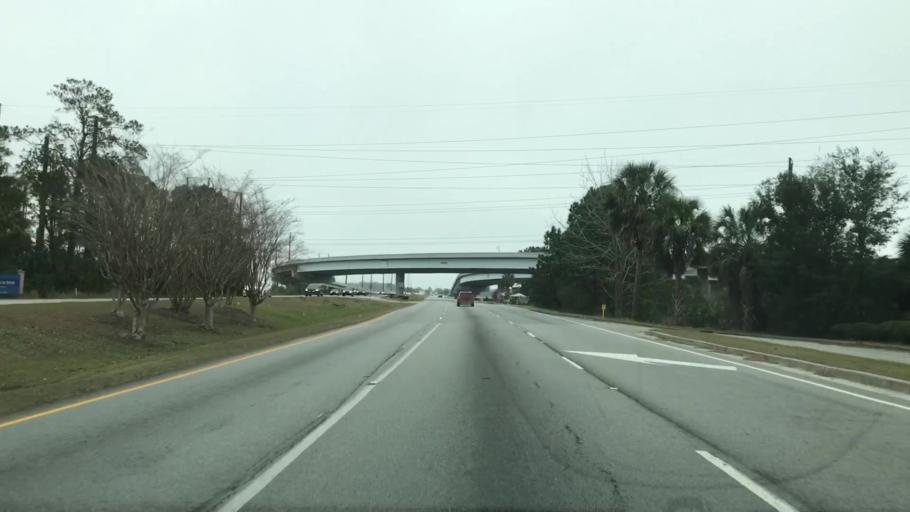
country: US
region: South Carolina
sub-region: Beaufort County
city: Bluffton
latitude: 32.2353
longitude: -80.8053
